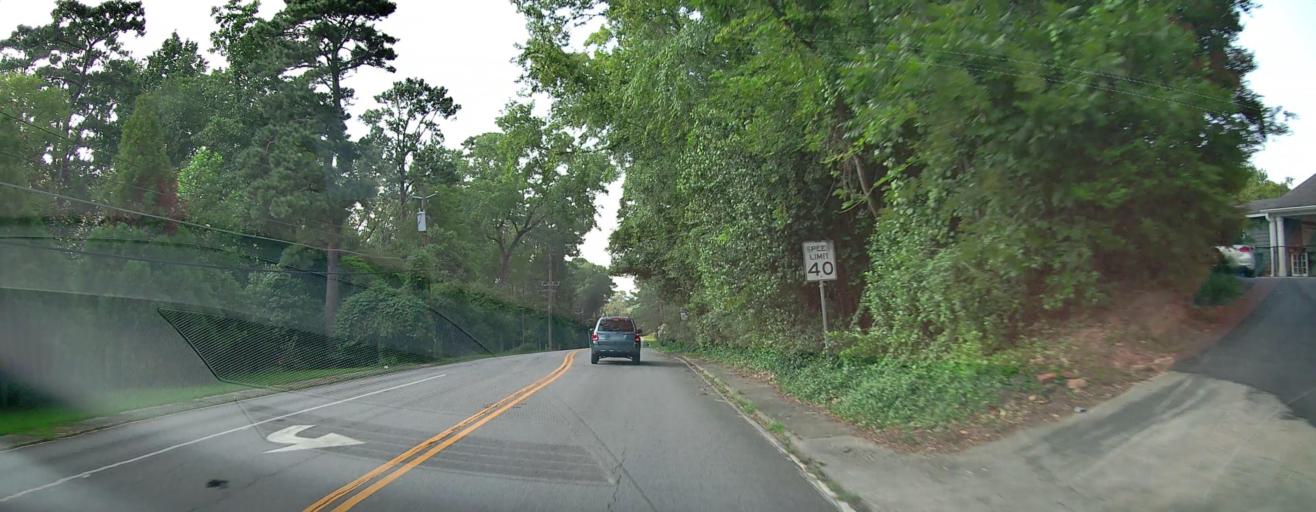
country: US
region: Georgia
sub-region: Bibb County
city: Macon
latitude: 32.8540
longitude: -83.6624
